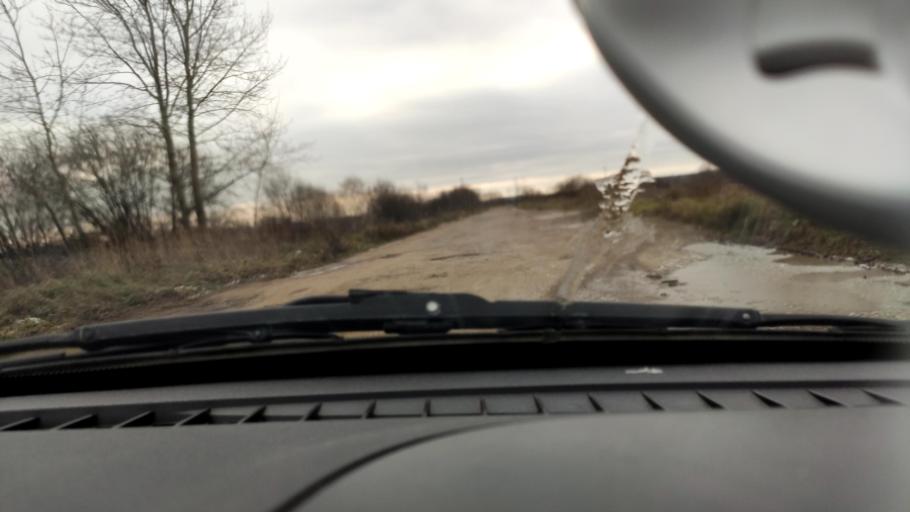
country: RU
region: Perm
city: Kondratovo
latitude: 57.9874
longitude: 56.0863
